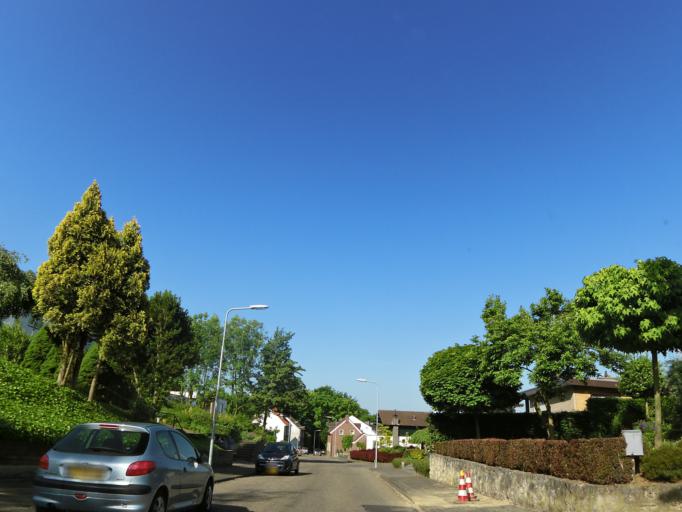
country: NL
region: Limburg
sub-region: Gemeente Voerendaal
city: Kunrade
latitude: 50.8741
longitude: 5.9334
